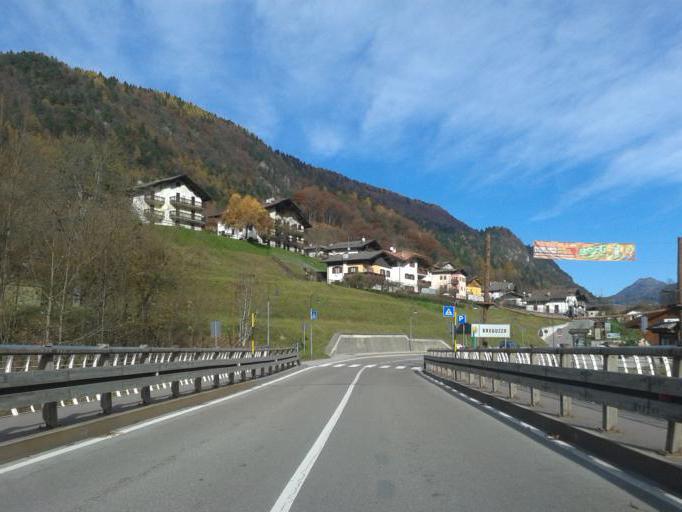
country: IT
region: Trentino-Alto Adige
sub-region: Provincia di Trento
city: Bondo
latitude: 46.0019
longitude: 10.6934
